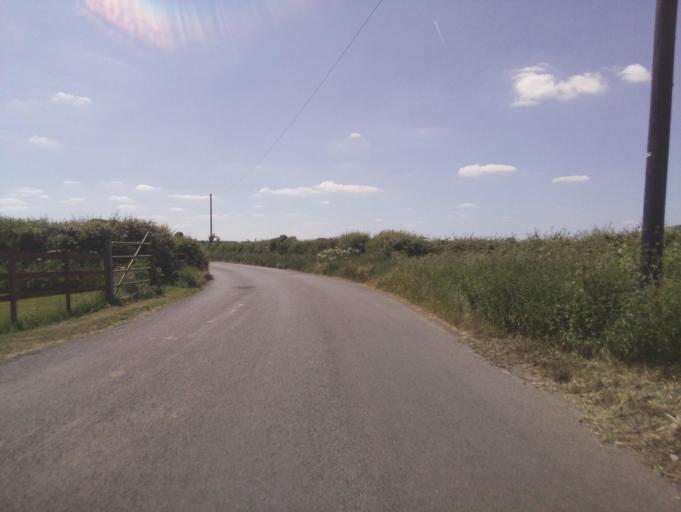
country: GB
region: England
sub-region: Wiltshire
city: Royal Wootton Bassett
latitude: 51.5005
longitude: -1.9121
